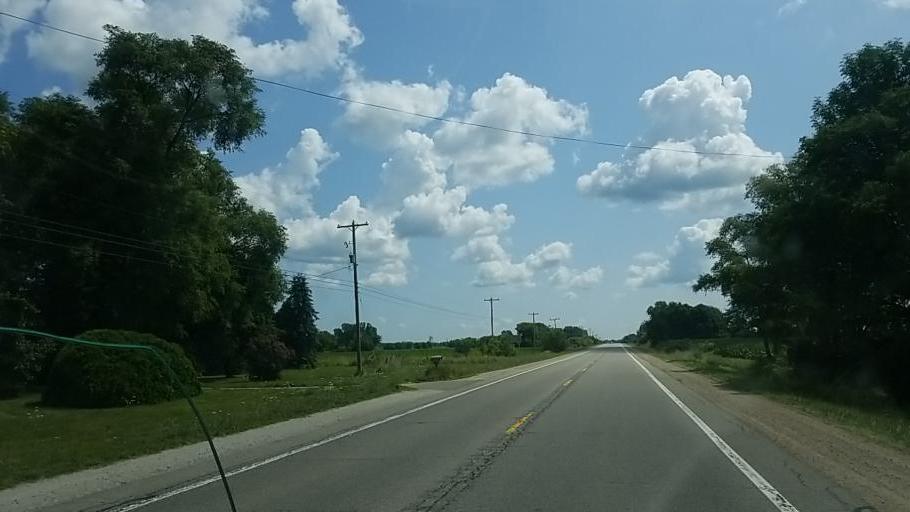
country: US
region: Michigan
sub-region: Muskegon County
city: Ravenna
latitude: 43.2352
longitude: -85.9264
